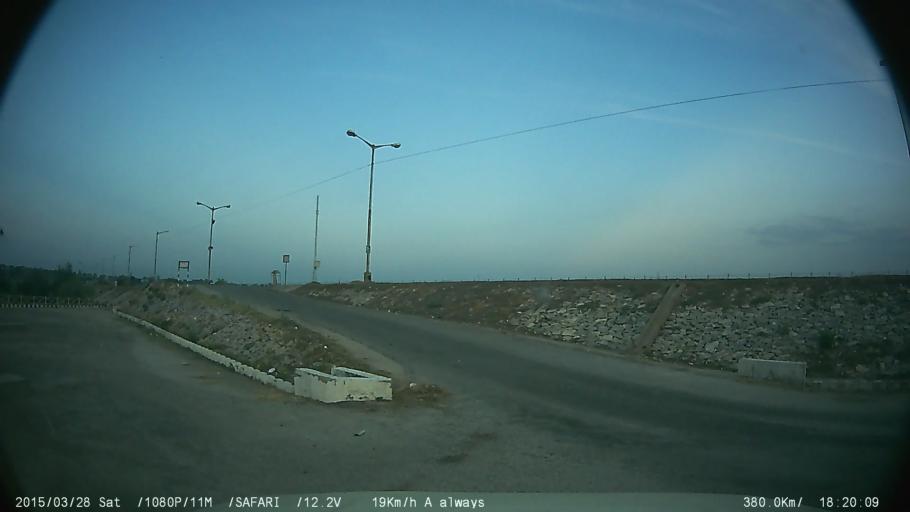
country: IN
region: Karnataka
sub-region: Mandya
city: Shrirangapattana
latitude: 12.4243
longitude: 76.5776
